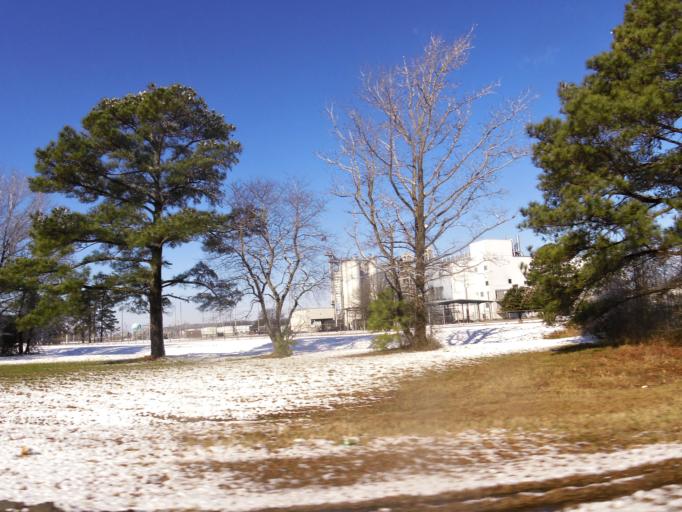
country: US
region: North Carolina
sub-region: Wilson County
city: Elm City
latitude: 35.7567
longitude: -77.8625
